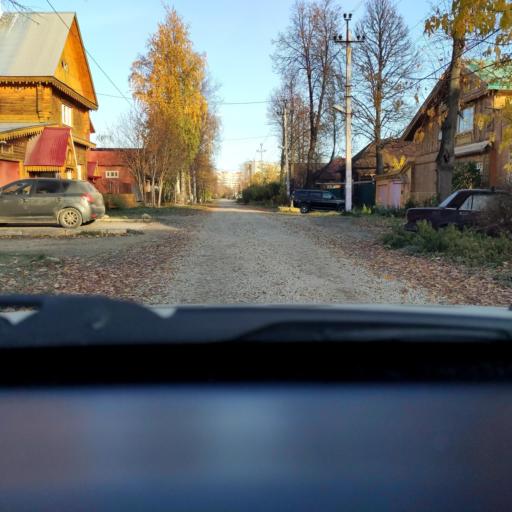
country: RU
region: Perm
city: Perm
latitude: 58.0246
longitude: 56.3283
